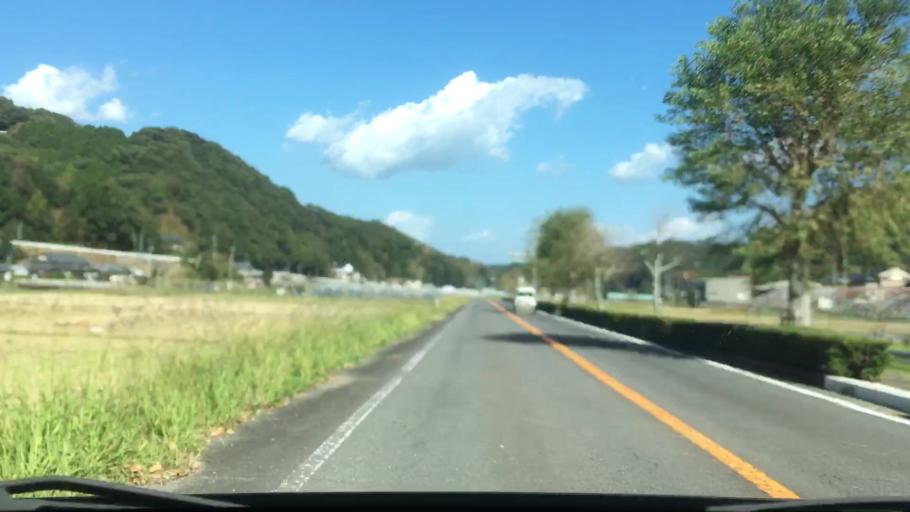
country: JP
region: Nagasaki
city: Sasebo
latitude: 32.9601
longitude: 129.6445
